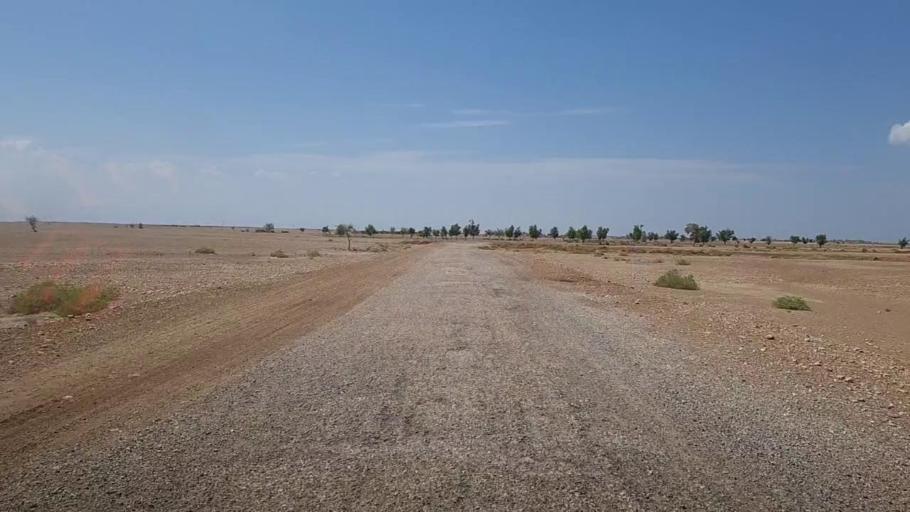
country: PK
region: Sindh
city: Sehwan
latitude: 26.3367
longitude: 67.6758
